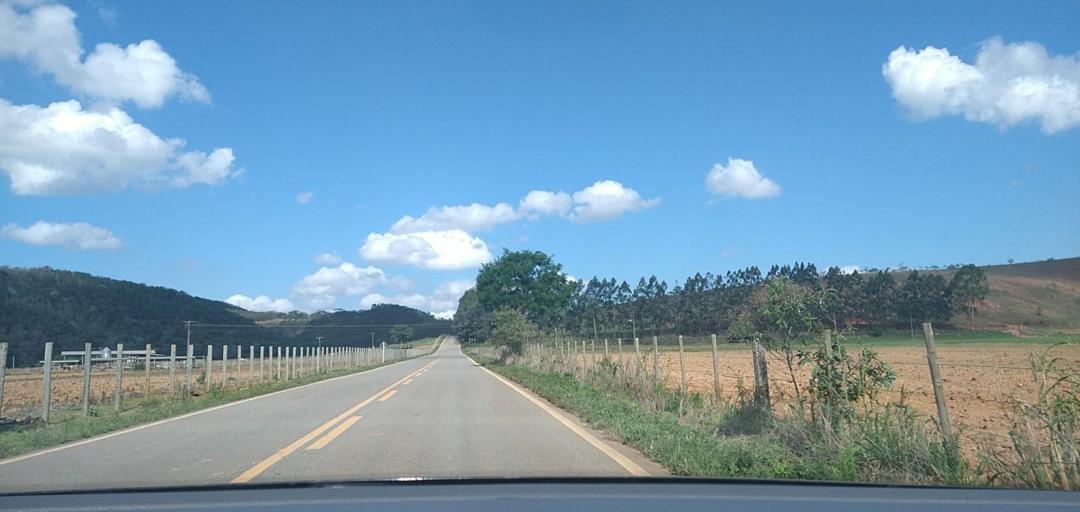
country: BR
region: Minas Gerais
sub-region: Alvinopolis
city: Alvinopolis
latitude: -20.0177
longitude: -43.0760
